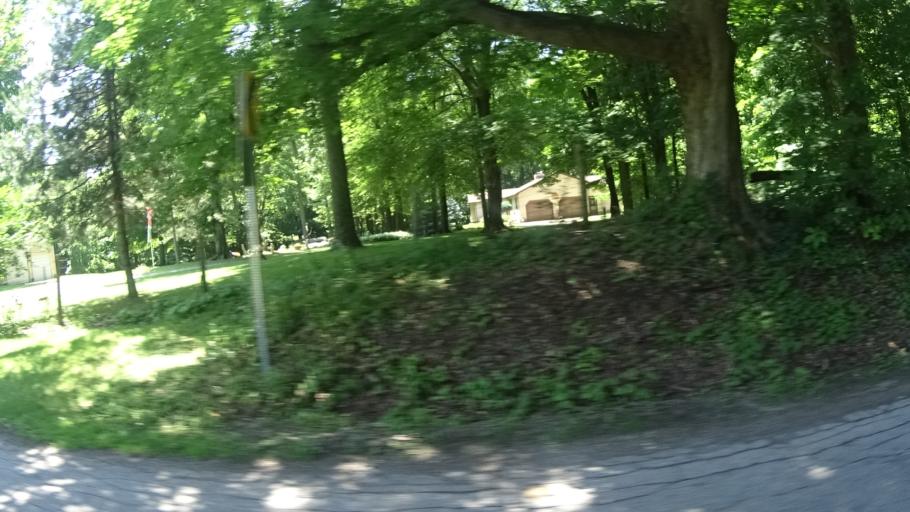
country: US
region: Ohio
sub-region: Lorain County
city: Vermilion
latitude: 41.3522
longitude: -82.3939
